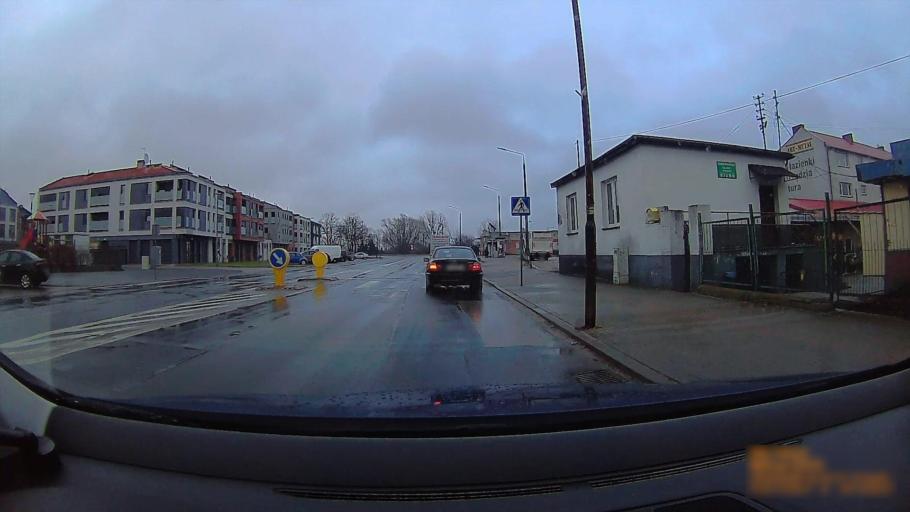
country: PL
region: Greater Poland Voivodeship
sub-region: Konin
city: Konin
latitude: 52.2085
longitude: 18.2563
